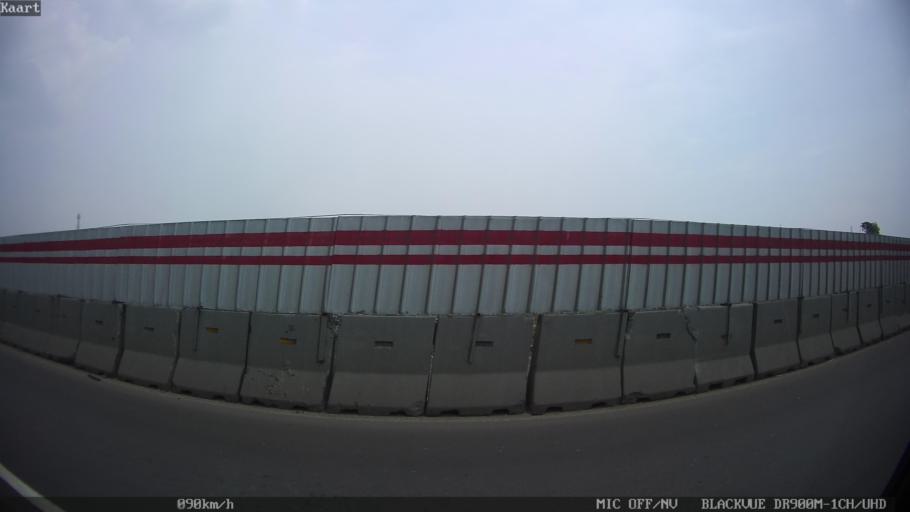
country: ID
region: West Java
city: Kresek
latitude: -6.1593
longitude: 106.3274
